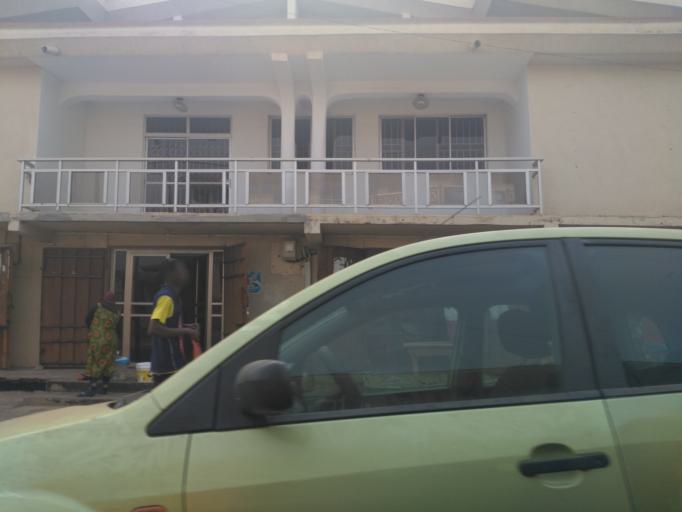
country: GH
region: Ashanti
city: Kumasi
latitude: 6.6871
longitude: -1.6103
